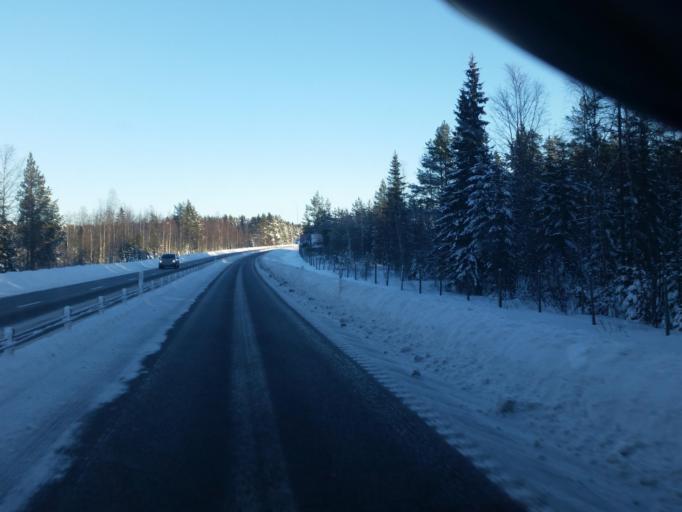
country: SE
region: Norrbotten
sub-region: Pitea Kommun
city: Hortlax
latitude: 65.0940
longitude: 21.4898
